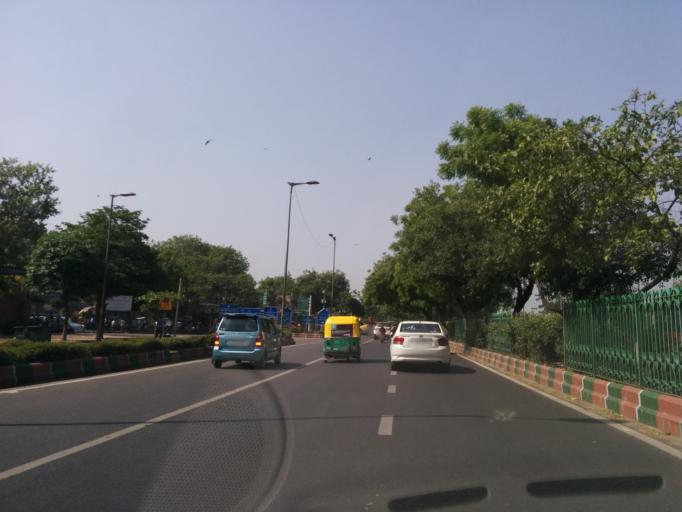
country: IN
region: NCT
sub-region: New Delhi
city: New Delhi
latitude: 28.5770
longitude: 77.2105
